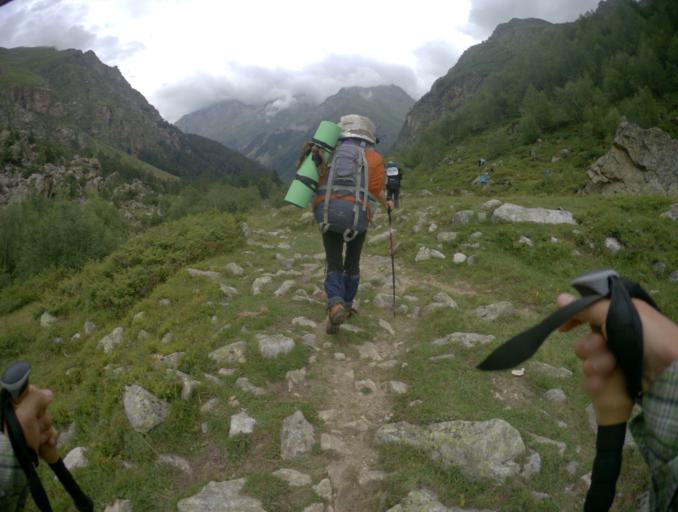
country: RU
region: Karachayevo-Cherkesiya
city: Uchkulan
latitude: 43.2683
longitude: 42.1485
